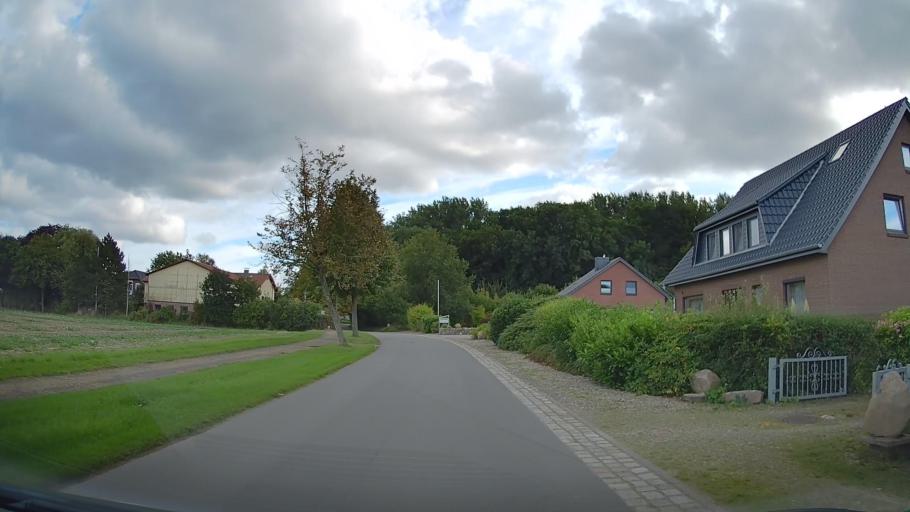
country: DE
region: Schleswig-Holstein
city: Steinberg
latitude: 54.7752
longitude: 9.8009
